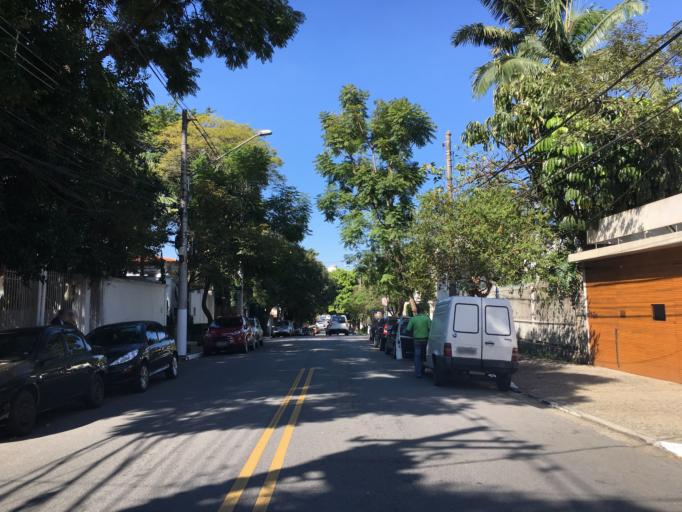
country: BR
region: Sao Paulo
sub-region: Sao Paulo
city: Sao Paulo
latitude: -23.5724
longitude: -46.6865
